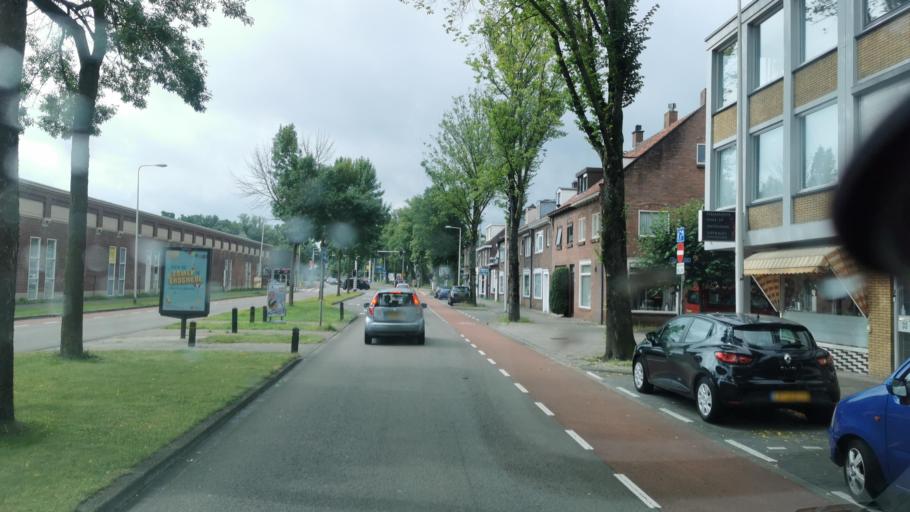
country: NL
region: Overijssel
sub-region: Gemeente Enschede
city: Enschede
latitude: 52.2242
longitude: 6.8787
